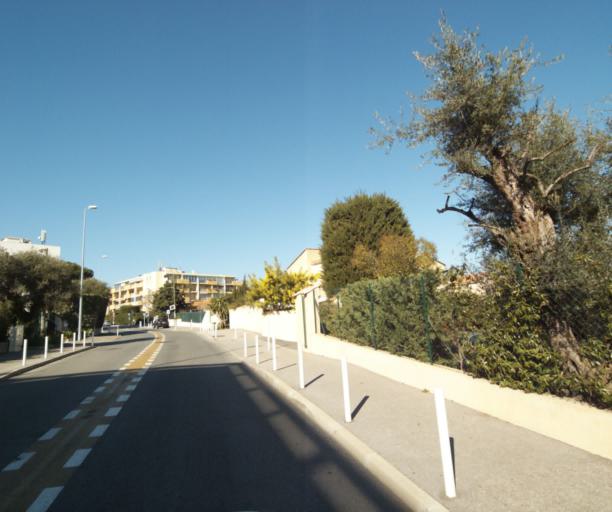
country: FR
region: Provence-Alpes-Cote d'Azur
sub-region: Departement des Alpes-Maritimes
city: Biot
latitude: 43.5967
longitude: 7.0983
